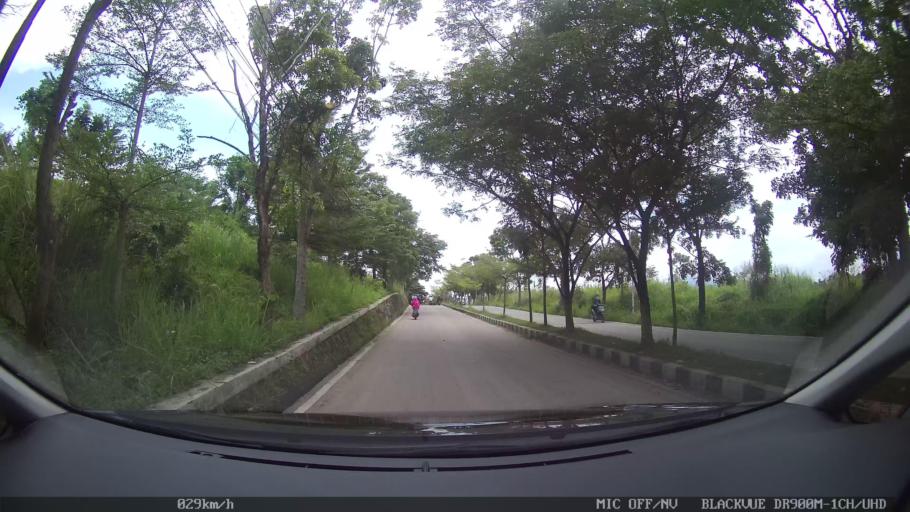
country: ID
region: Lampung
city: Kedaton
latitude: -5.3811
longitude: 105.2114
